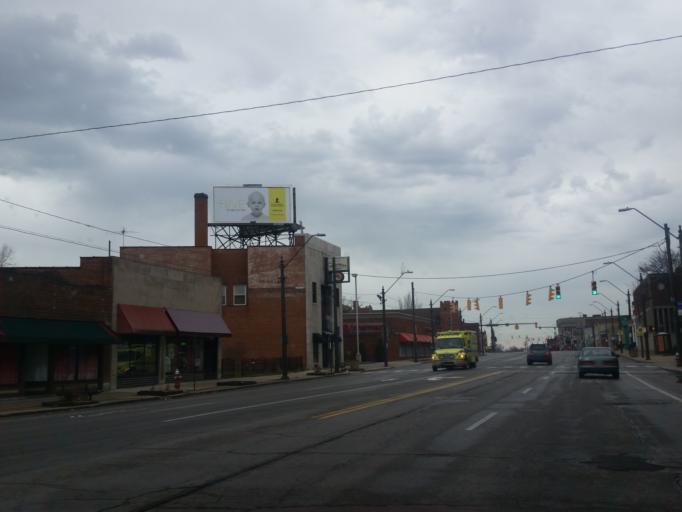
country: US
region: Ohio
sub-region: Cuyahoga County
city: Brooklyn Heights
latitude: 41.4394
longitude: -81.7066
